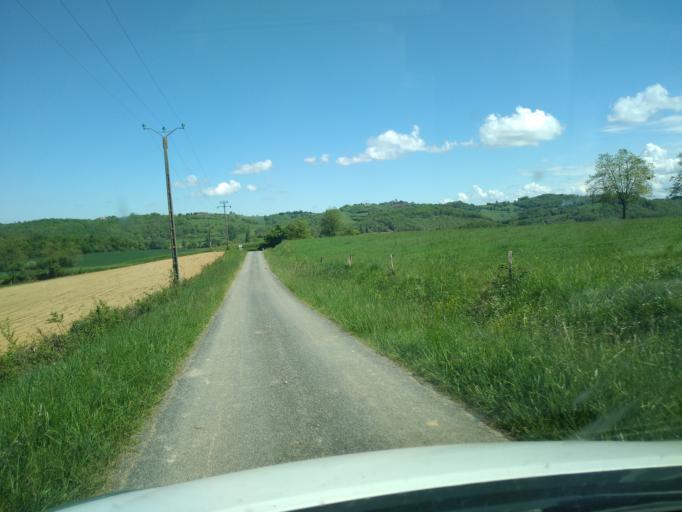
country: FR
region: Midi-Pyrenees
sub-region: Departement de la Haute-Garonne
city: Boulogne-sur-Gesse
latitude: 43.3039
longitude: 0.6729
